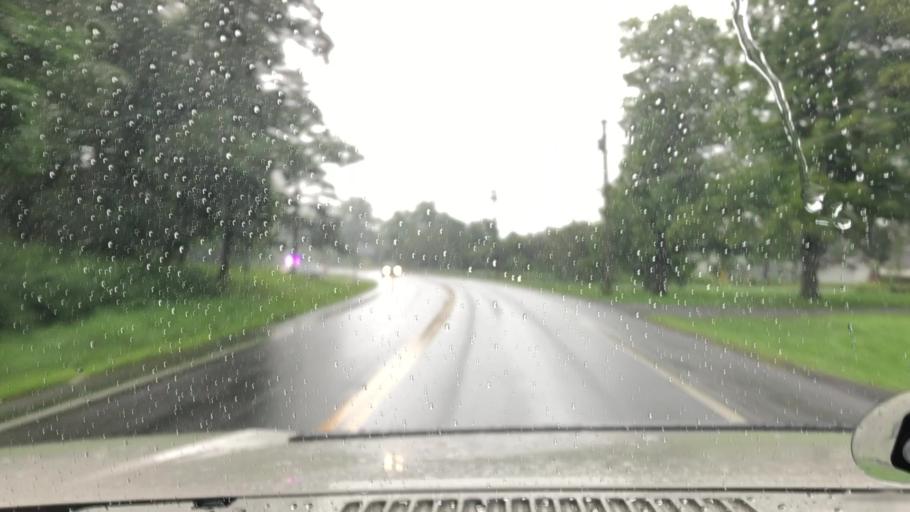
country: US
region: New York
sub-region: Greene County
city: Palenville
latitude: 42.2056
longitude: -73.9835
